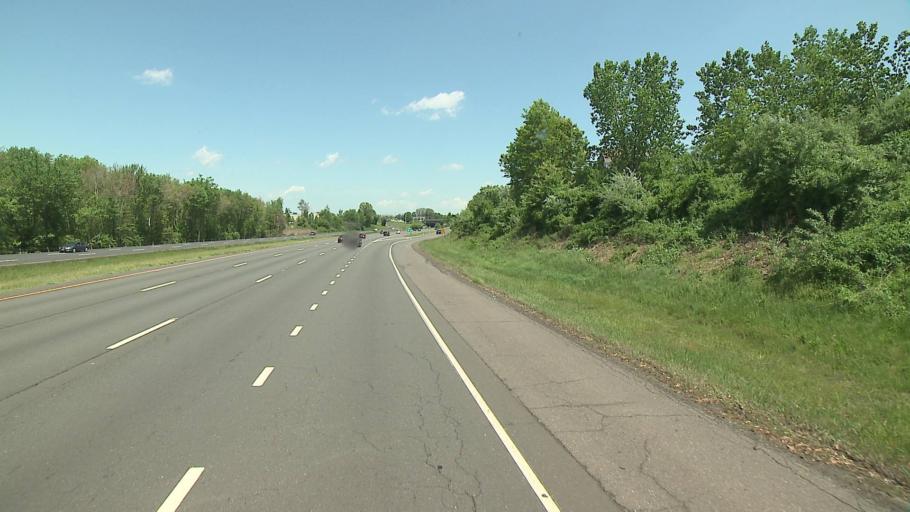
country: US
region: Connecticut
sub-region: Hartford County
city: Plainville
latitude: 41.6077
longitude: -72.9010
